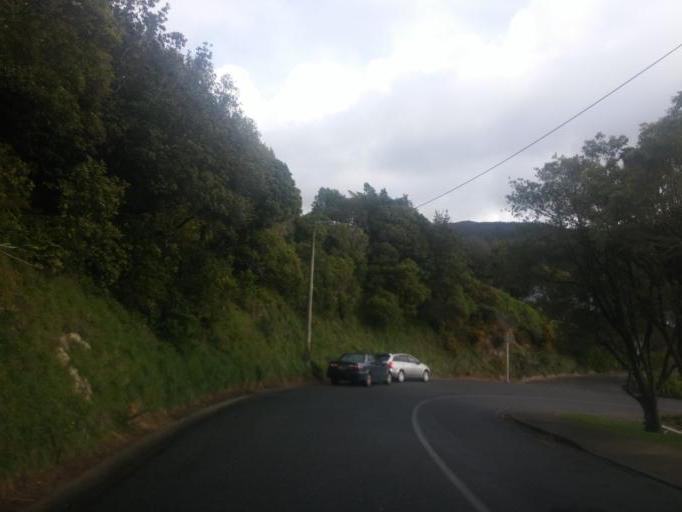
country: NZ
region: Wellington
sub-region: Wellington City
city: Kelburn
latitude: -41.2716
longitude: 174.7587
